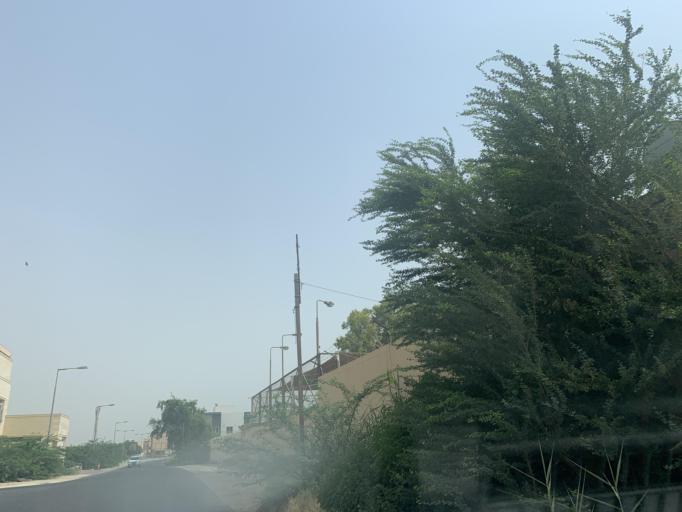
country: BH
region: Manama
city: Jidd Hafs
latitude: 26.2006
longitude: 50.4627
